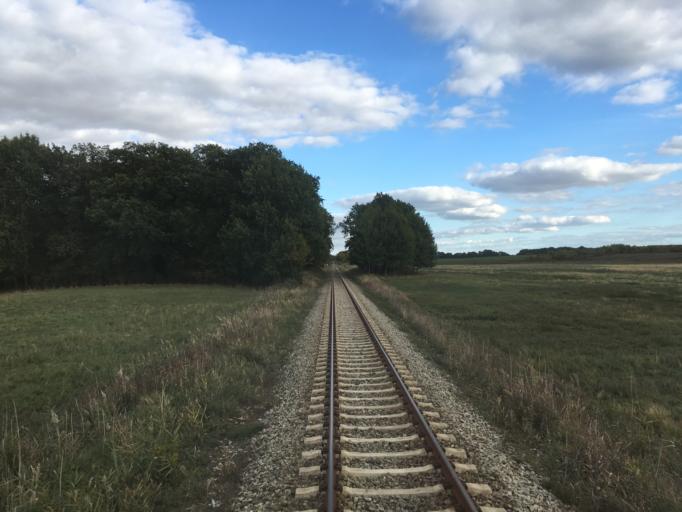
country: DE
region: Mecklenburg-Vorpommern
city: Grabowhofe
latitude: 53.5418
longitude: 12.5880
